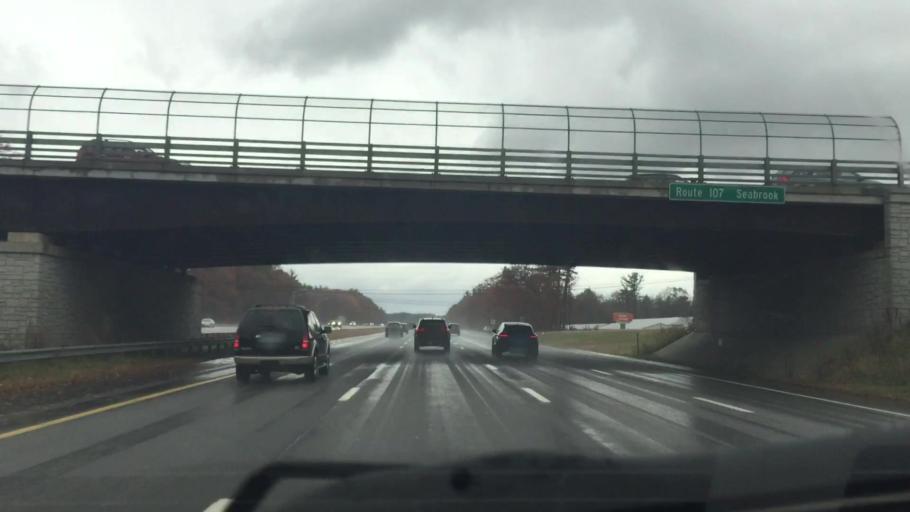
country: US
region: New Hampshire
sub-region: Rockingham County
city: Seabrook
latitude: 42.8943
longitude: -70.8798
